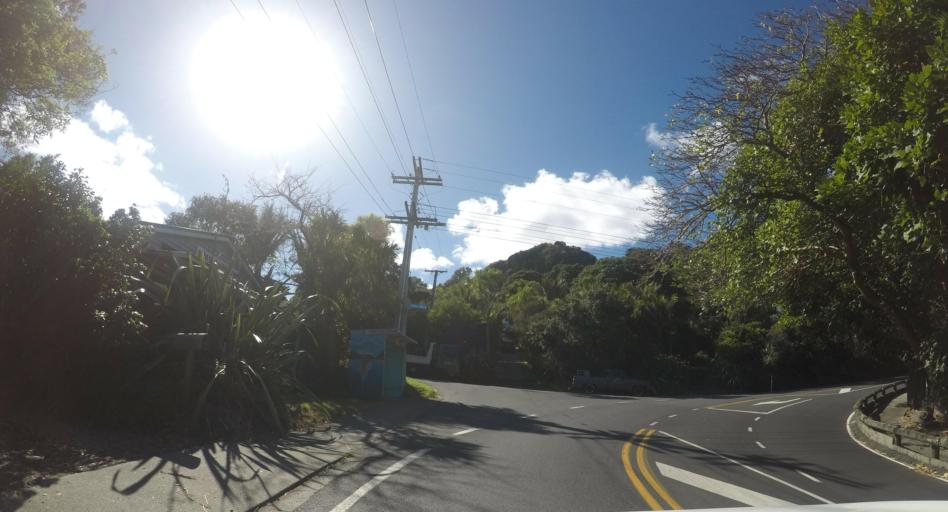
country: NZ
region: Auckland
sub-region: Auckland
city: Muriwai Beach
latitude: -36.9568
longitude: 174.4798
